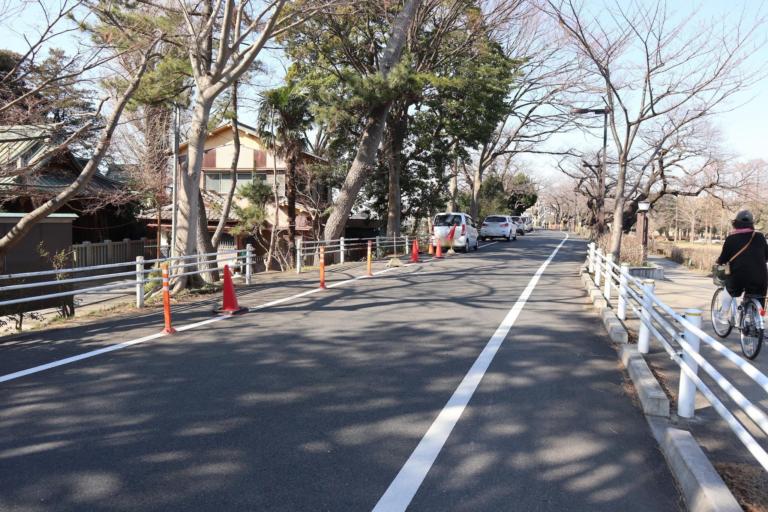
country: JP
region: Chiba
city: Matsudo
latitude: 35.7829
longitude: 139.8698
